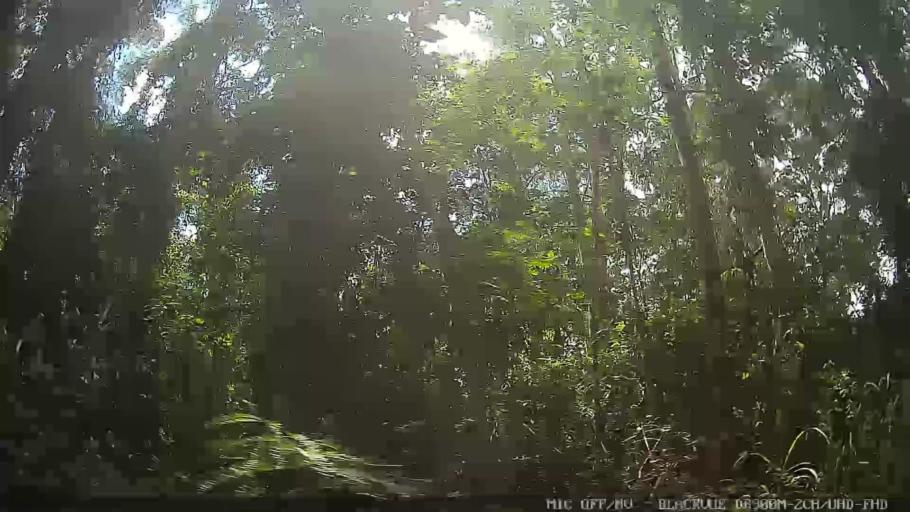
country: BR
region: Sao Paulo
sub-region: Atibaia
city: Atibaia
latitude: -23.1451
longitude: -46.6421
